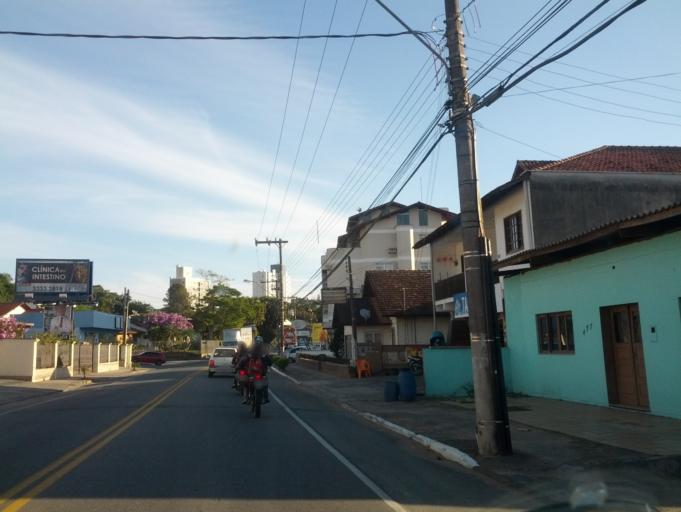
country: BR
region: Santa Catarina
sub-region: Indaial
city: Indaial
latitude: -26.8928
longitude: -49.2267
